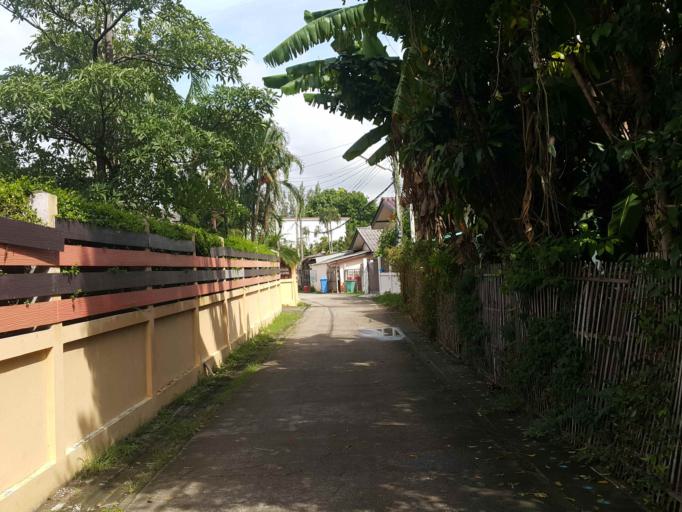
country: TH
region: Chiang Mai
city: San Kamphaeng
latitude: 18.7639
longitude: 99.0743
